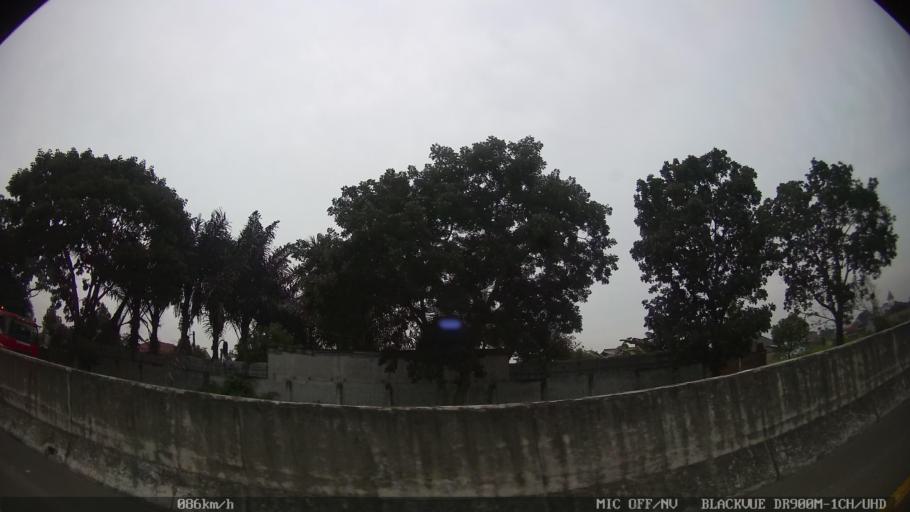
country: ID
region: North Sumatra
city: Medan
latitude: 3.5652
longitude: 98.7258
